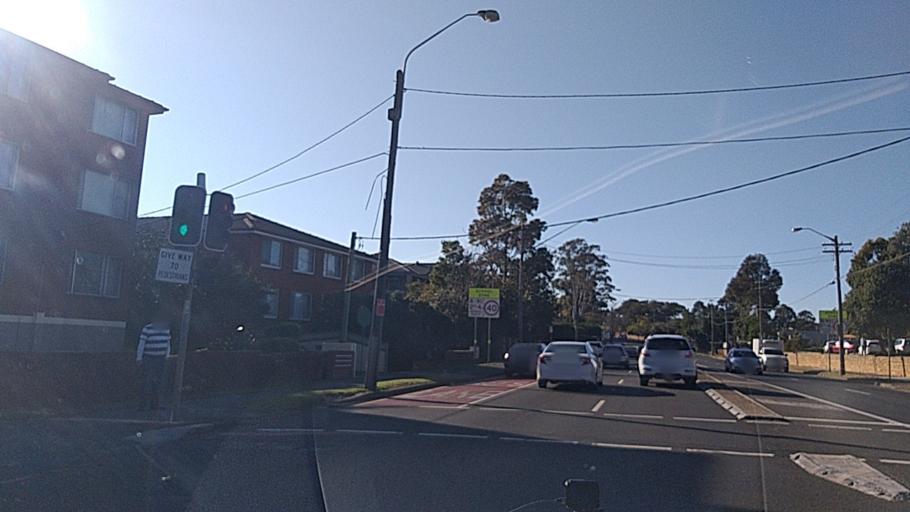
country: AU
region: New South Wales
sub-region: Ryde
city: East Ryde
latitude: -33.8180
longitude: 151.1141
